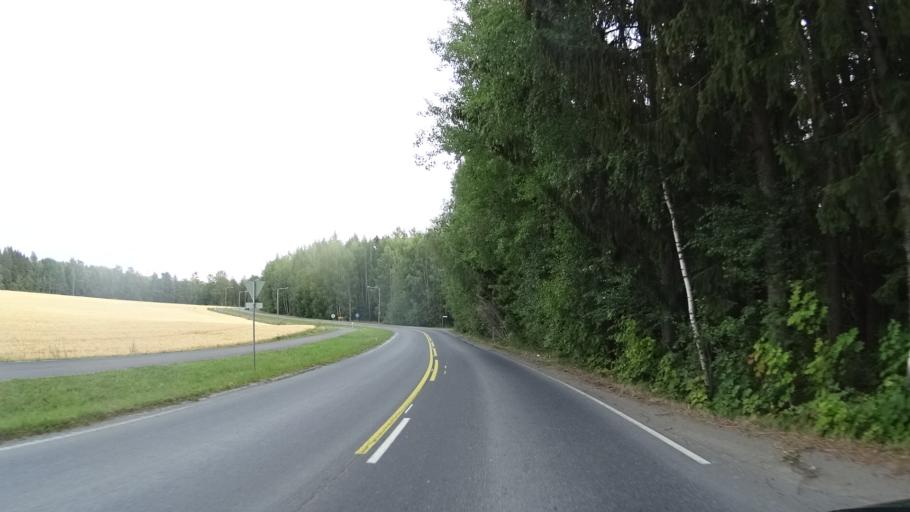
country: FI
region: Haeme
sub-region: Haemeenlinna
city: Parola
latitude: 61.0402
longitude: 24.3474
